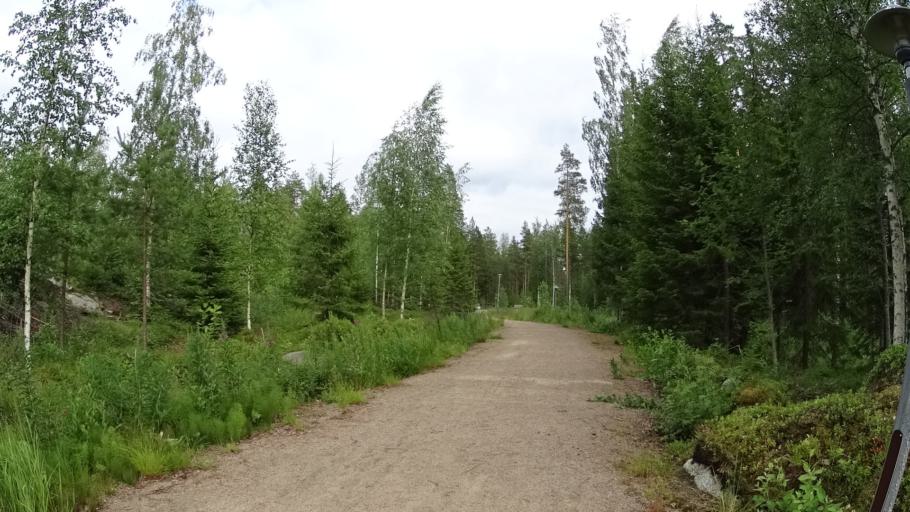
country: FI
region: Southern Ostrobothnia
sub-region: Kuusiokunnat
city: AEhtaeri
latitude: 62.5311
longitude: 24.1883
